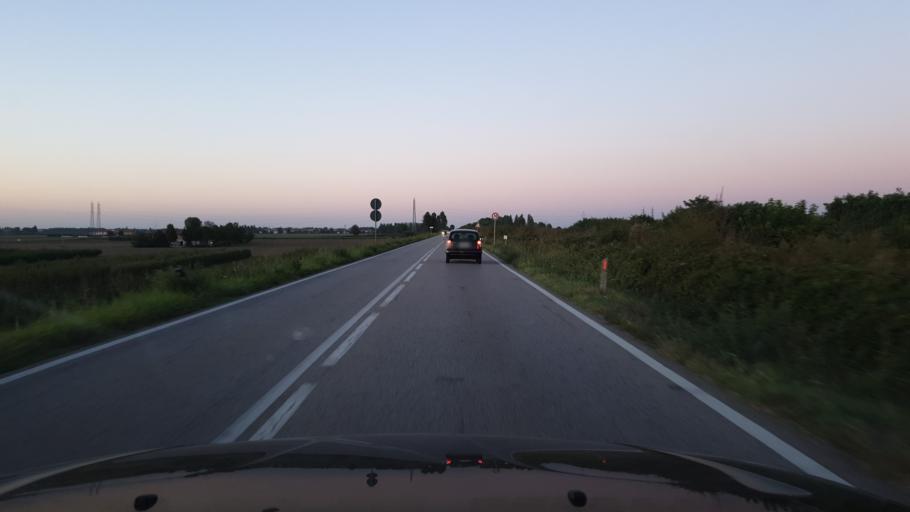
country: IT
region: Emilia-Romagna
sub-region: Provincia di Bologna
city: Minerbio
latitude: 44.6411
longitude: 11.4741
